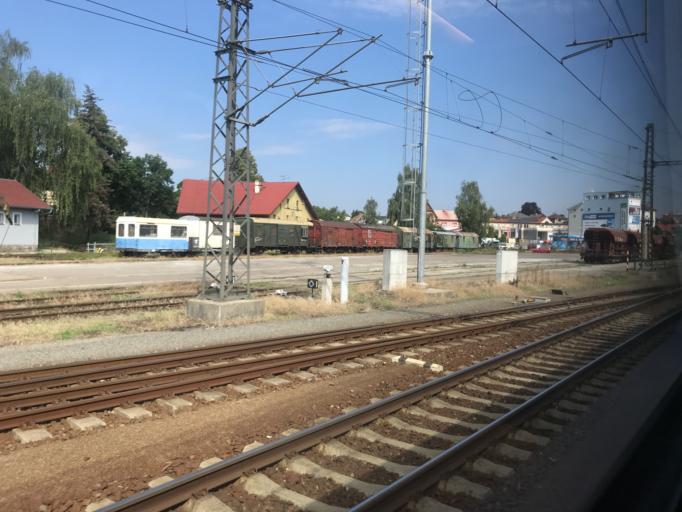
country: CZ
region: Central Bohemia
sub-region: Okres Benesov
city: Benesov
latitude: 49.7804
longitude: 14.6822
